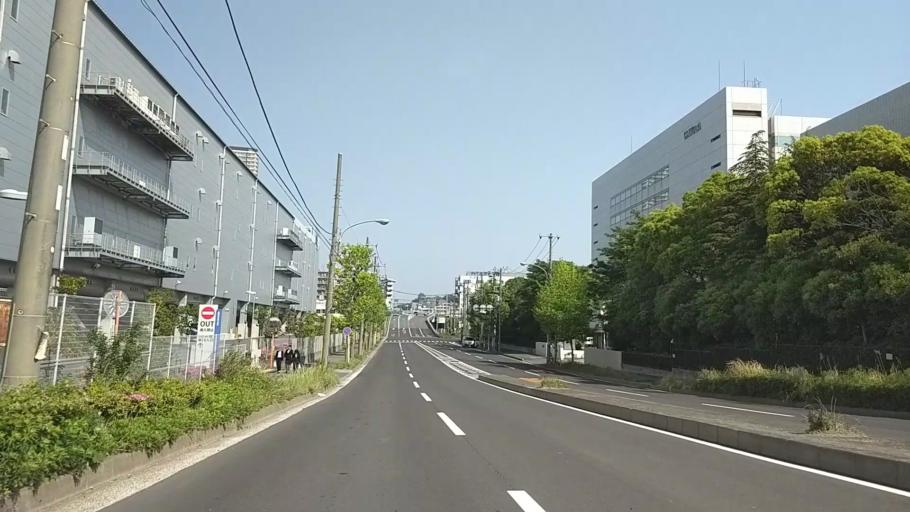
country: JP
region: Kanagawa
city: Yokohama
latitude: 35.4829
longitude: 139.6566
